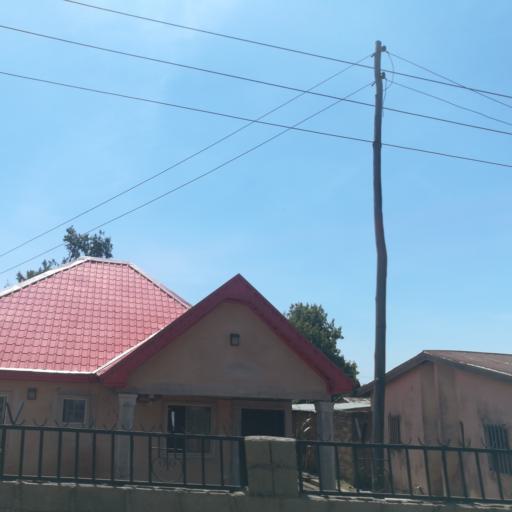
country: NG
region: Plateau
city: Bukuru
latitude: 9.7872
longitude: 8.8775
